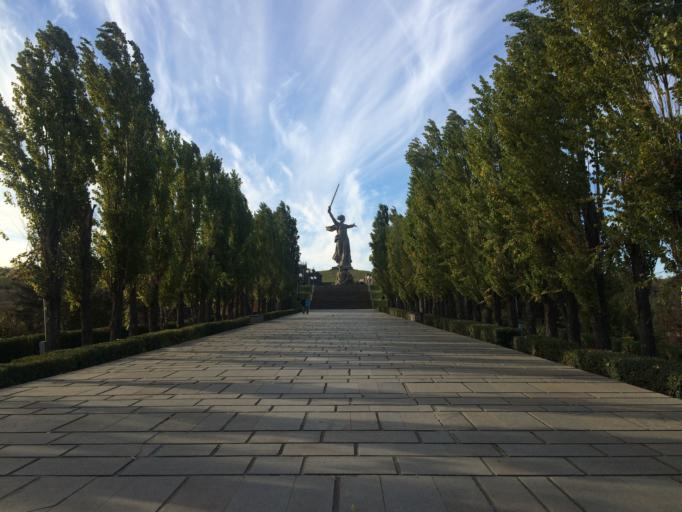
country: RU
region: Volgograd
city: Krasnoslobodsk
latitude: 48.7400
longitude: 44.5441
